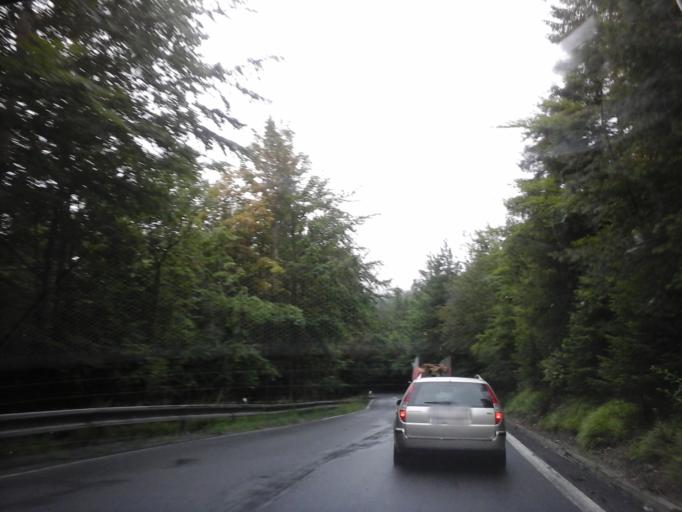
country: SK
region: Kosicky
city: Dobsina
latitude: 48.9044
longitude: 20.2527
